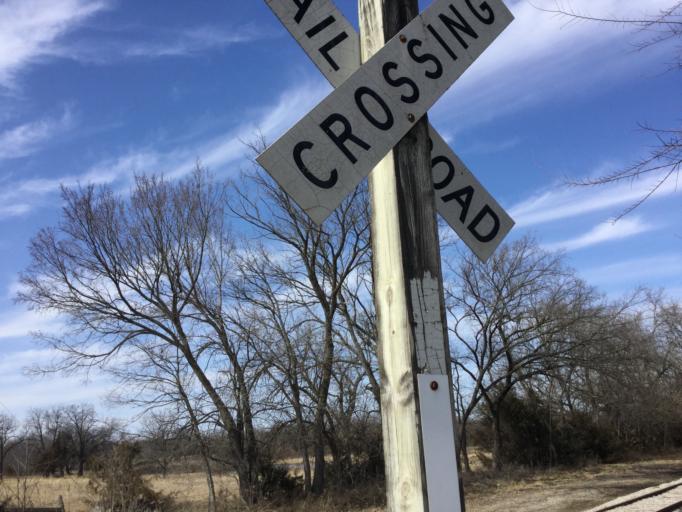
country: US
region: Kansas
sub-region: Douglas County
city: Baldwin City
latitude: 38.7096
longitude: -95.2469
